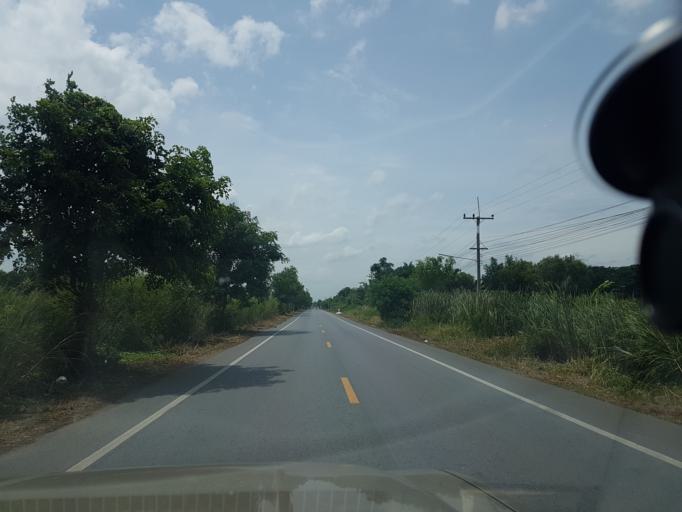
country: TH
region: Pathum Thani
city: Nong Suea
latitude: 14.2022
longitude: 100.8921
